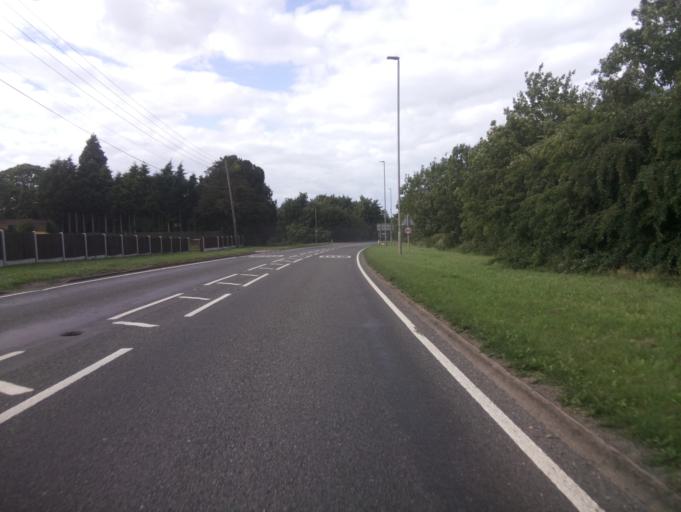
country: GB
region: England
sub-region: Leicestershire
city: Donisthorpe
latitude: 52.6780
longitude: -1.5454
